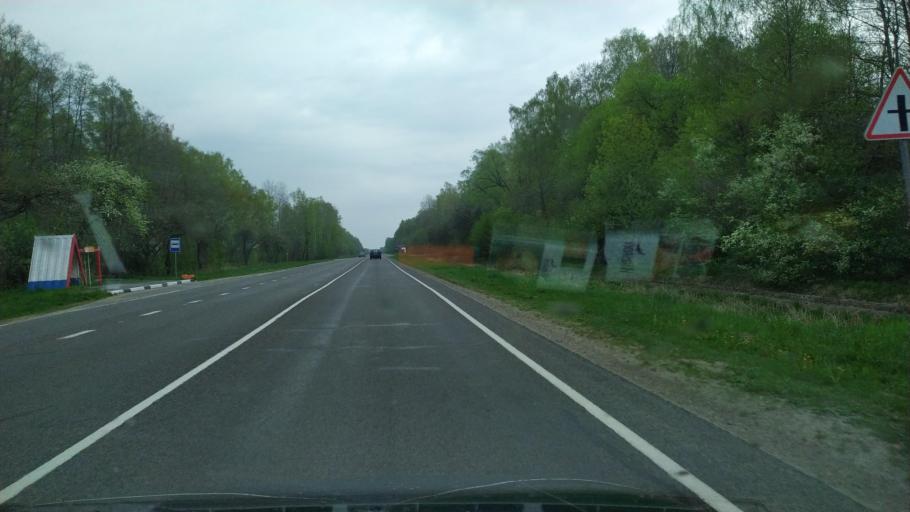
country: BY
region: Brest
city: Horad Kobryn
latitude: 52.3106
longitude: 24.5397
